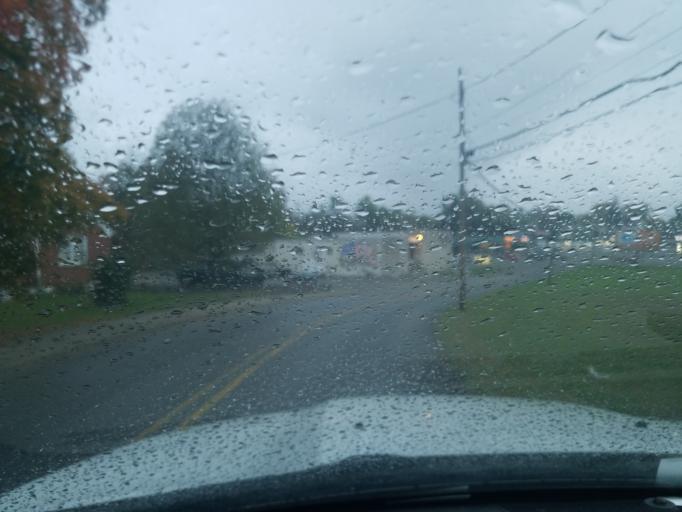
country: US
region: Indiana
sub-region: Floyd County
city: New Albany
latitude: 38.3048
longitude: -85.8203
